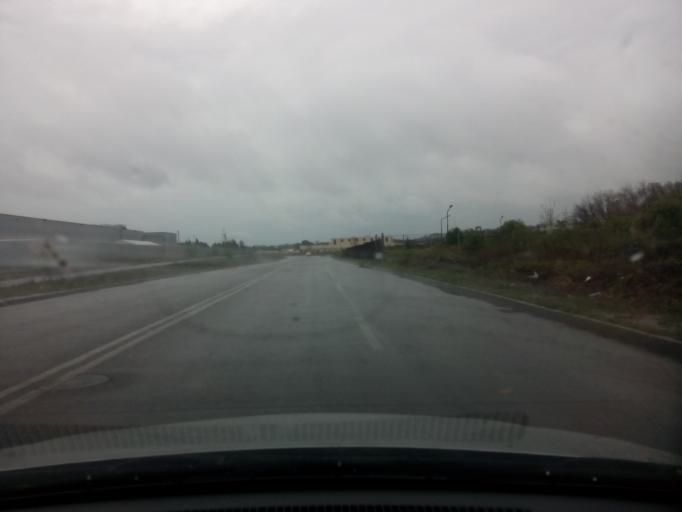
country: RO
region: Ilfov
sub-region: Comuna Otopeni
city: Otopeni
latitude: 44.5095
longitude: 26.0909
